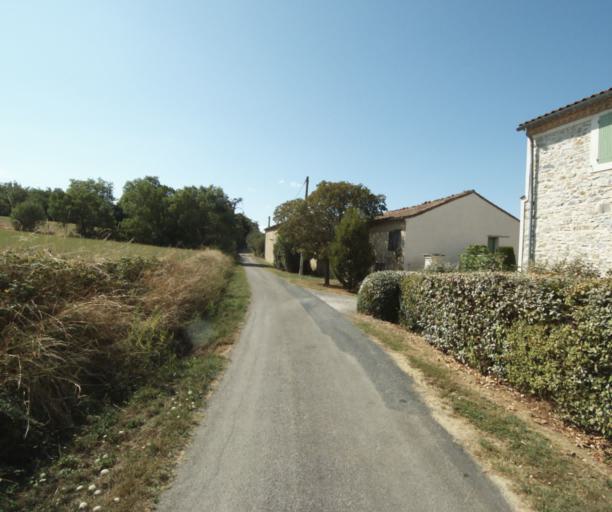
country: FR
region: Midi-Pyrenees
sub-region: Departement de la Haute-Garonne
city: Revel
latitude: 43.4856
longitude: 1.9964
